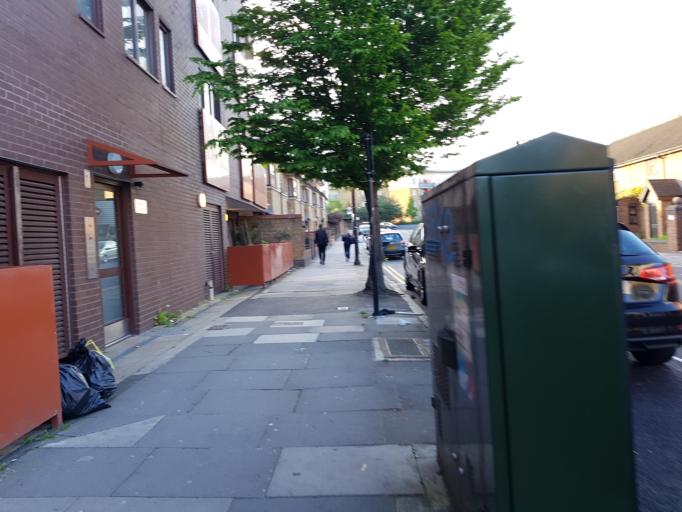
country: GB
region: England
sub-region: Greater London
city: Poplar
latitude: 51.5320
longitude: -0.0234
